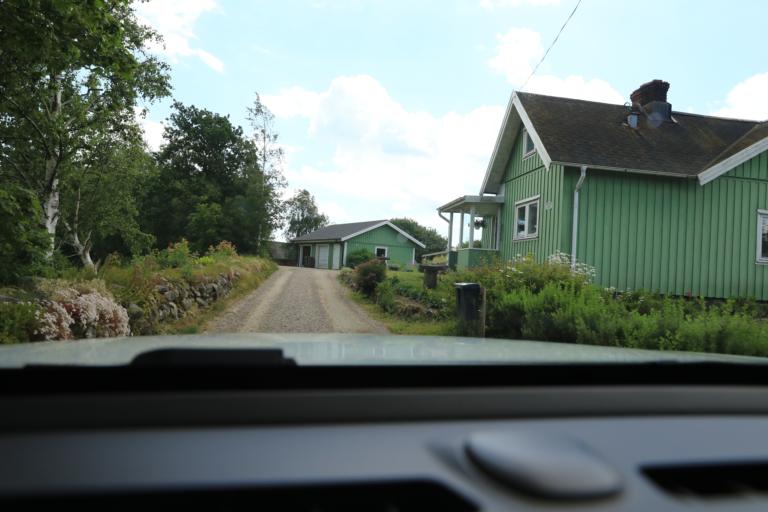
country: SE
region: Halland
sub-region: Varbergs Kommun
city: Tvaaker
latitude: 57.1093
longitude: 12.4135
